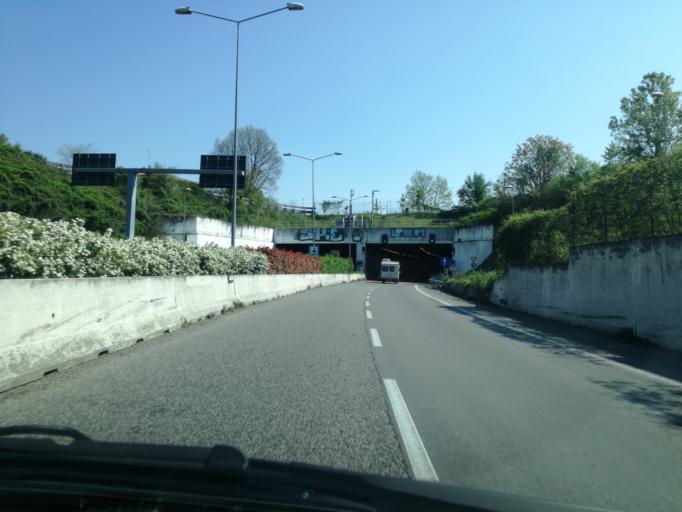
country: IT
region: Lombardy
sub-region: Provincia di Bergamo
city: Presezzo
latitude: 45.6839
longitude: 9.5718
